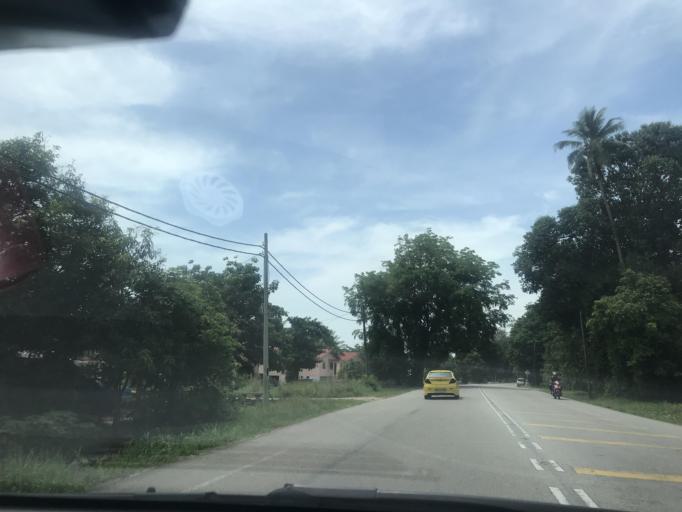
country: MY
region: Kelantan
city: Tumpat
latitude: 6.2104
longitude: 102.1342
